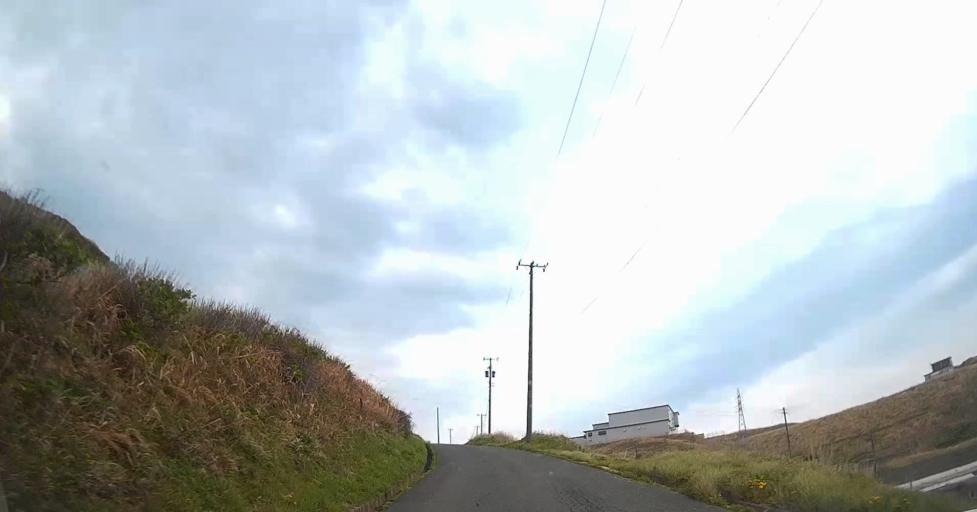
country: JP
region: Aomori
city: Shimokizukuri
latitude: 41.2532
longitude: 140.3426
